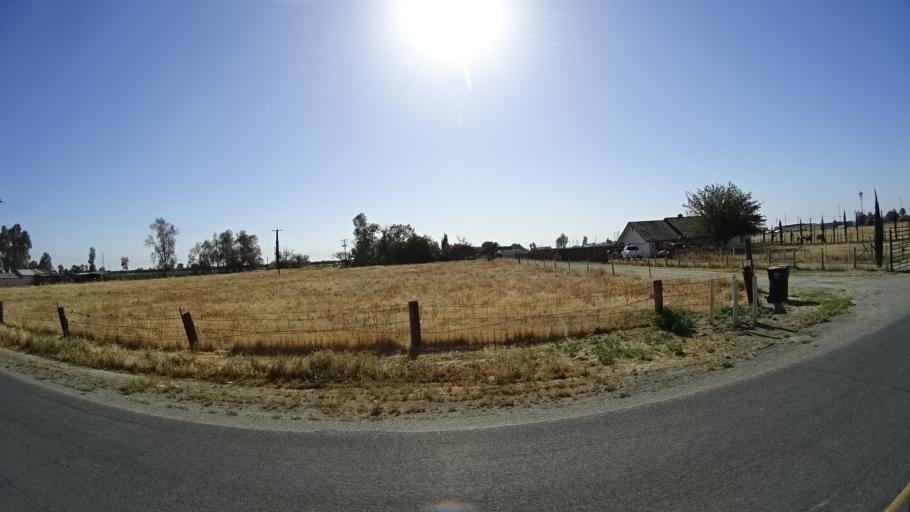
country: US
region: California
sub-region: Kings County
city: Corcoran
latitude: 36.1118
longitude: -119.5632
